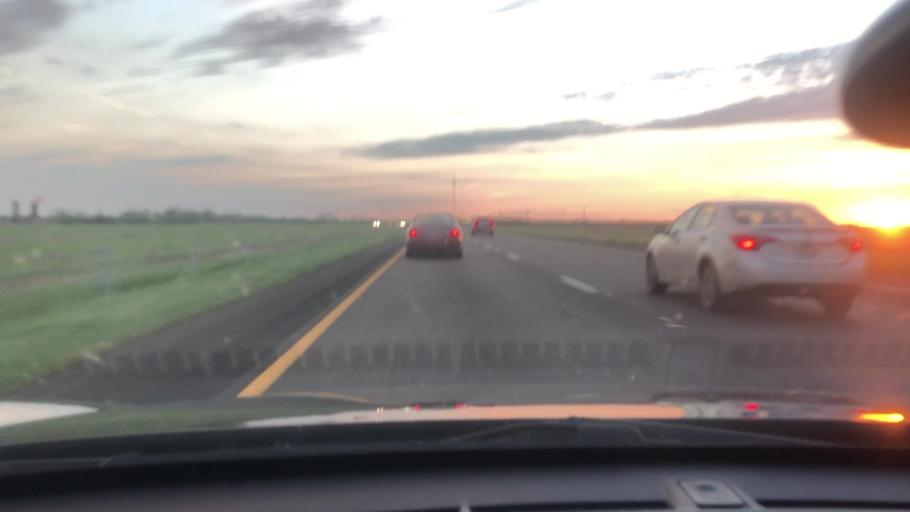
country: US
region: Texas
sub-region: Victoria County
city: Inez
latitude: 28.9315
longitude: -96.7400
